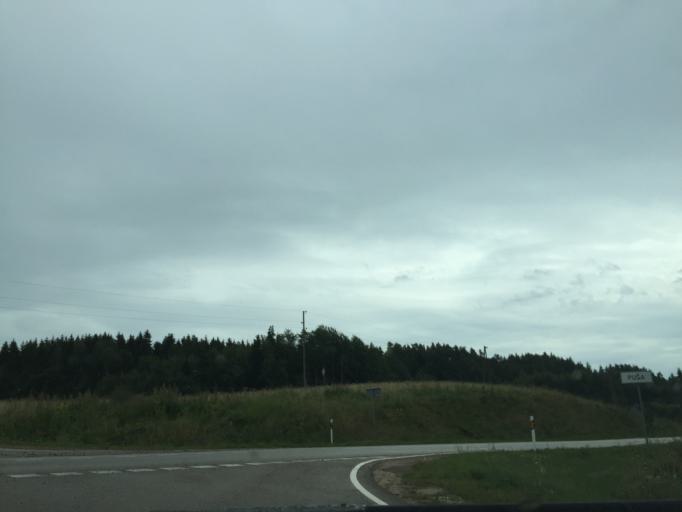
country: LV
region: Preilu Rajons
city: Jaunaglona
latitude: 56.2503
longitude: 27.2159
